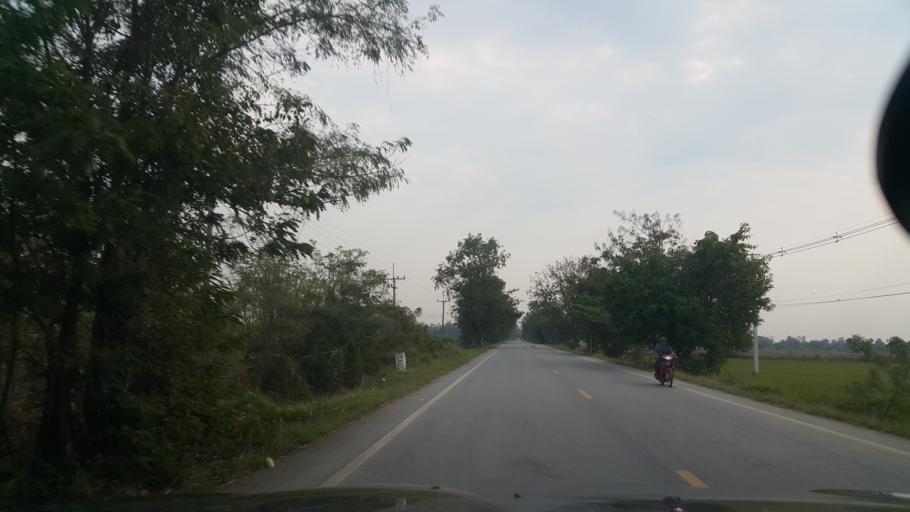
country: TH
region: Sukhothai
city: Si Samrong
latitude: 17.1703
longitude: 99.7191
